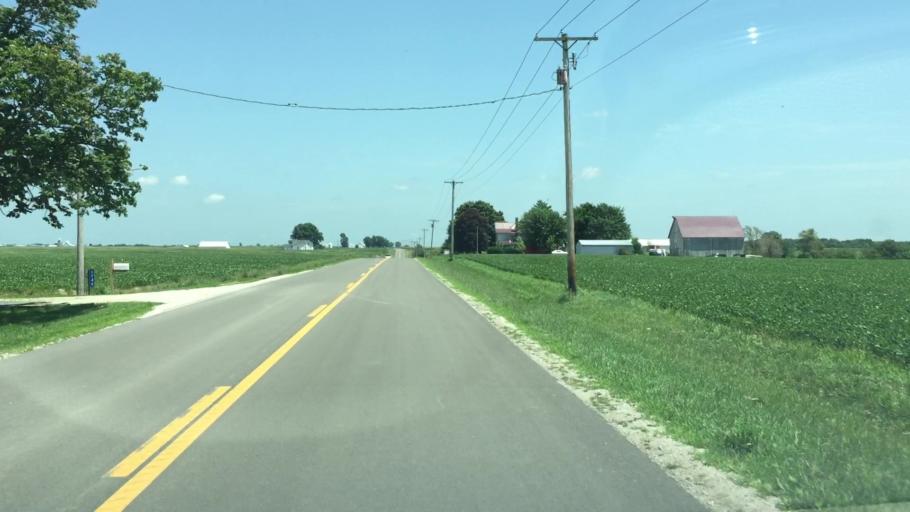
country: US
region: Illinois
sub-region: Hancock County
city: Carthage
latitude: 40.3278
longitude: -91.1718
